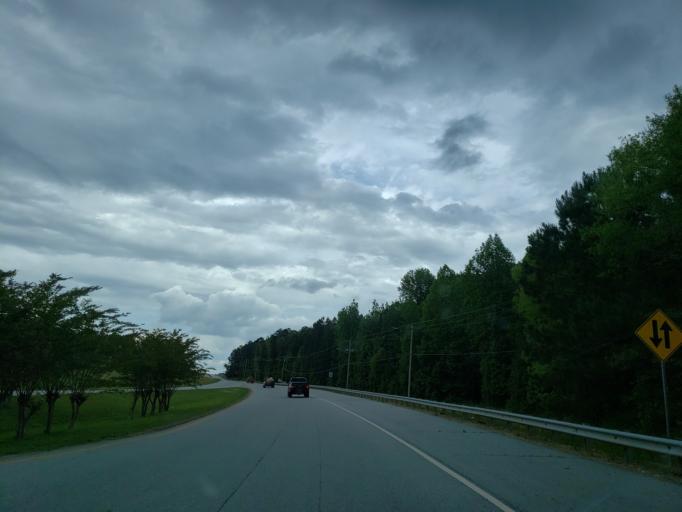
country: US
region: Georgia
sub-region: Haralson County
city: Bremen
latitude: 33.6920
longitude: -85.1480
